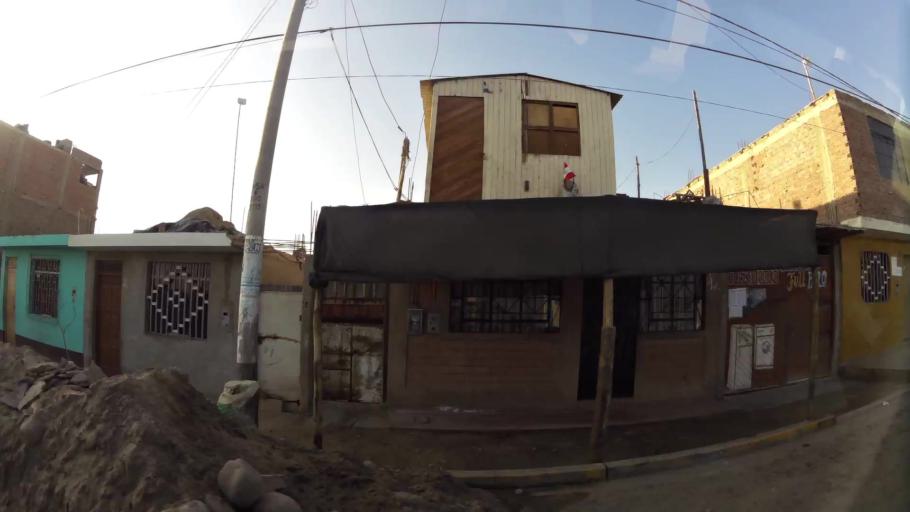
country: PE
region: Ica
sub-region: Provincia de Pisco
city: Villa Tupac Amaru
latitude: -13.7073
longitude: -76.1485
